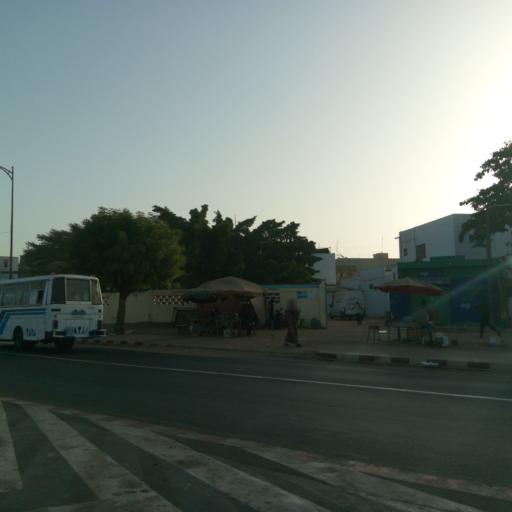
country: SN
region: Dakar
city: Dakar
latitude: 14.6926
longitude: -17.4477
